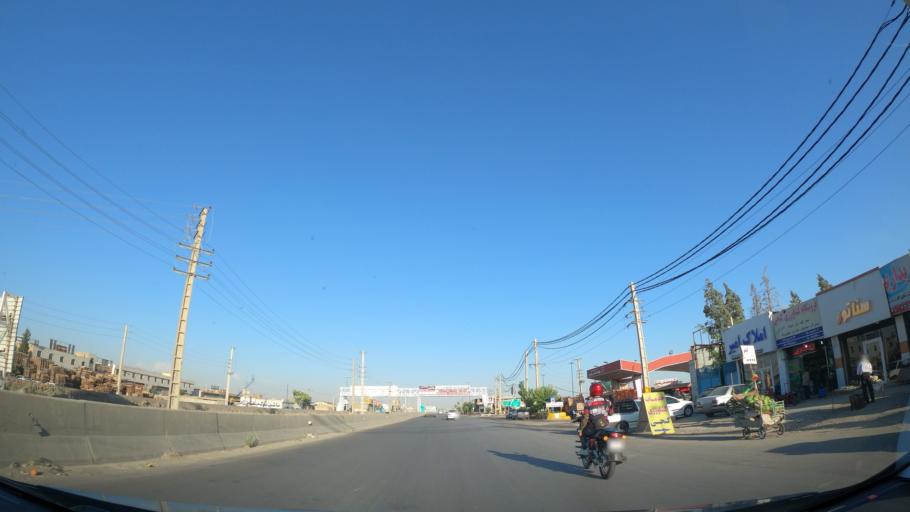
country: IR
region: Alborz
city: Hashtgerd
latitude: 35.9179
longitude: 50.7529
